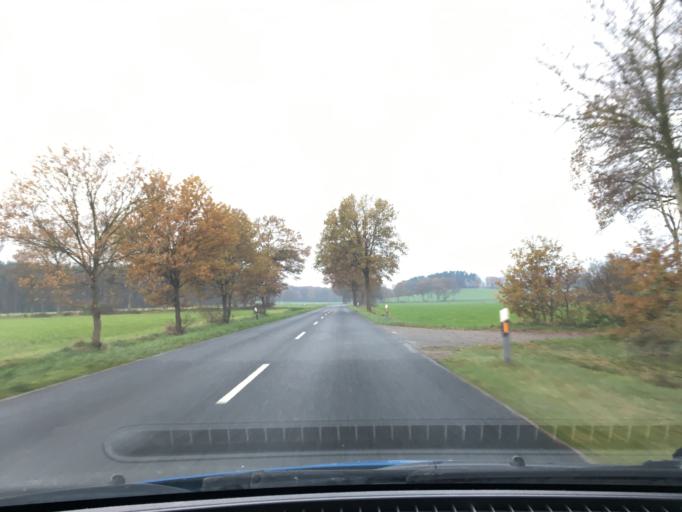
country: DE
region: Lower Saxony
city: Oldendorf
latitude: 53.1760
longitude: 10.2003
